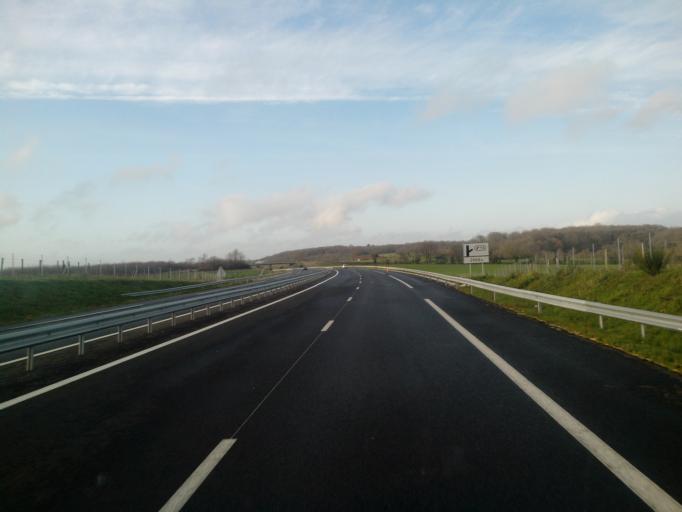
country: FR
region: Poitou-Charentes
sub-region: Departement des Deux-Sevres
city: Nueil-les-Aubiers
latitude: 46.8864
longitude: -0.6034
